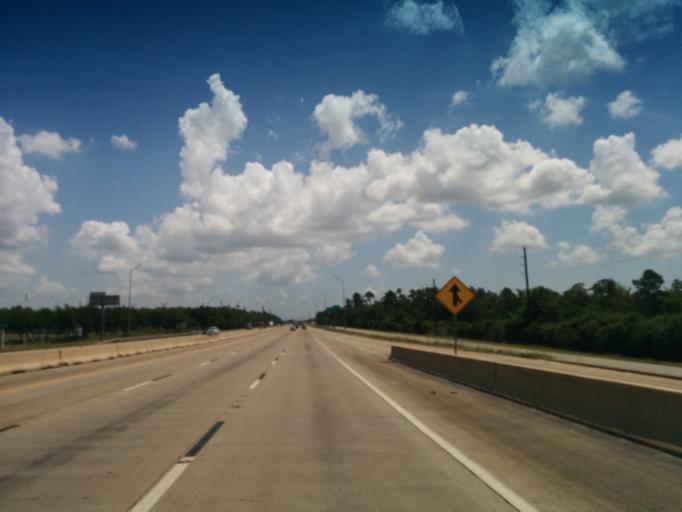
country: US
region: Texas
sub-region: Chambers County
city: Mont Belvieu
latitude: 29.8139
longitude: -94.9352
